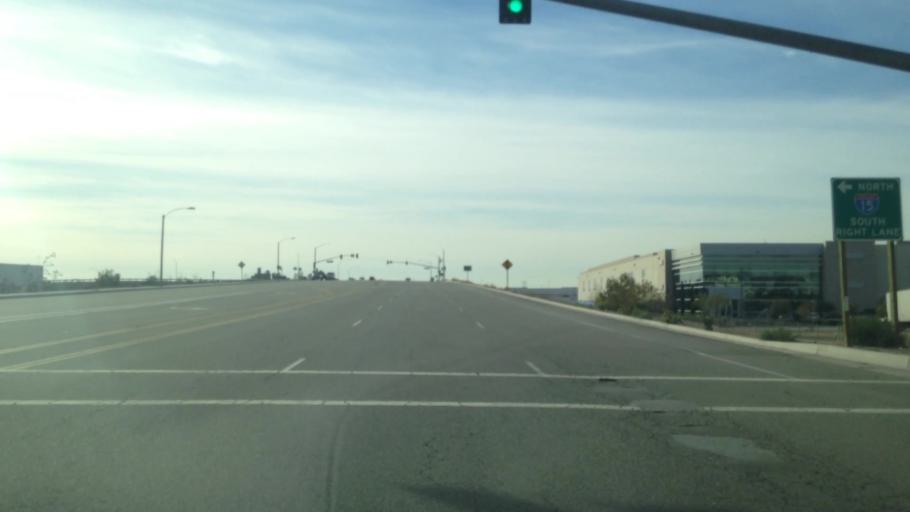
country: US
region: California
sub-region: Riverside County
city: Mira Loma
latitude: 34.0037
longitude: -117.5458
